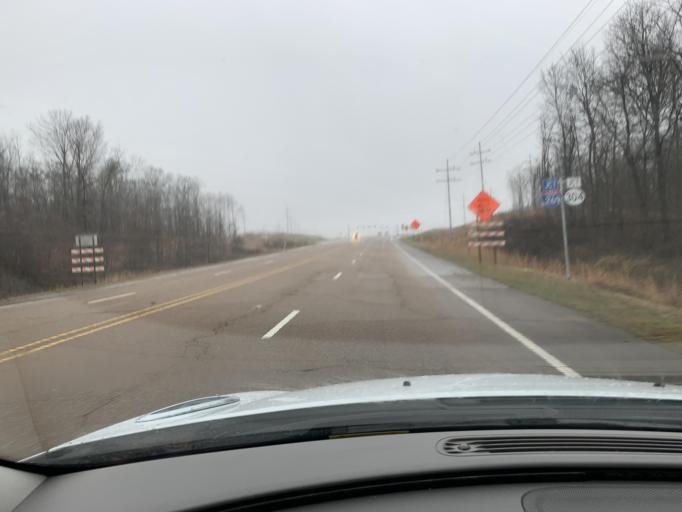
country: US
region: Mississippi
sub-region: De Soto County
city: Hernando
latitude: 34.8684
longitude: -89.9704
